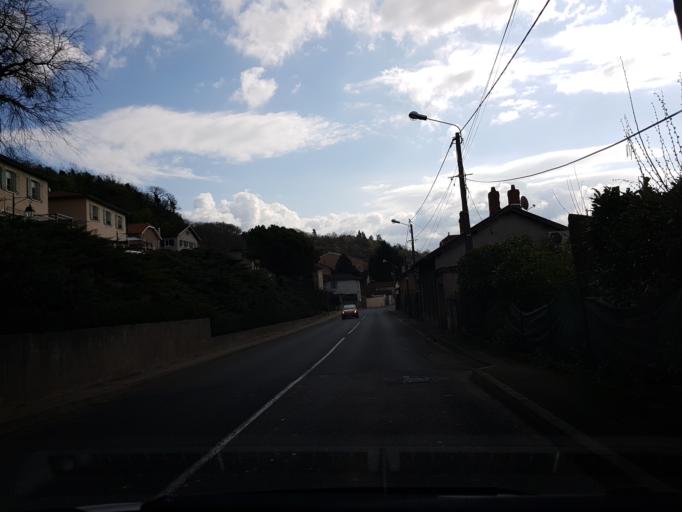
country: FR
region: Rhone-Alpes
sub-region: Departement de l'Ain
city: Trevoux
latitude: 45.9416
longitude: 4.7656
